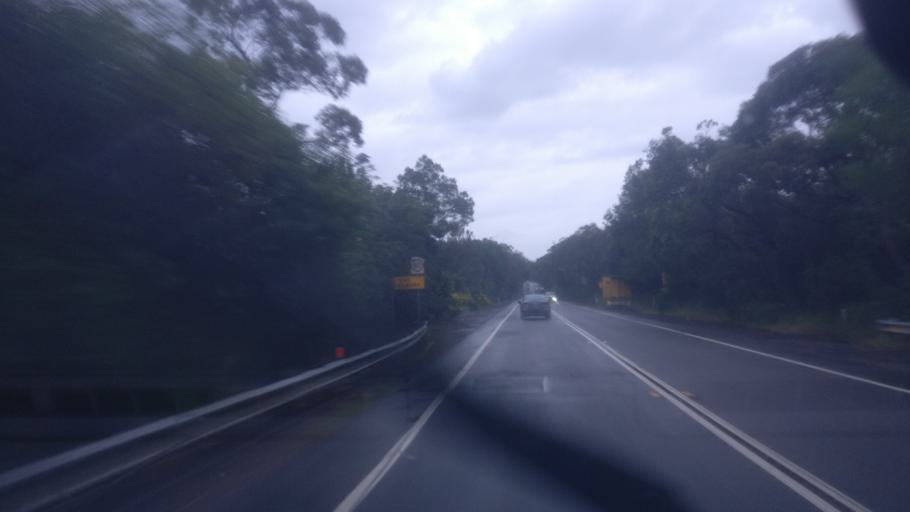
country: AU
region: New South Wales
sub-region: Warringah
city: Allambie Heights
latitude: -33.7435
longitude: 151.2374
